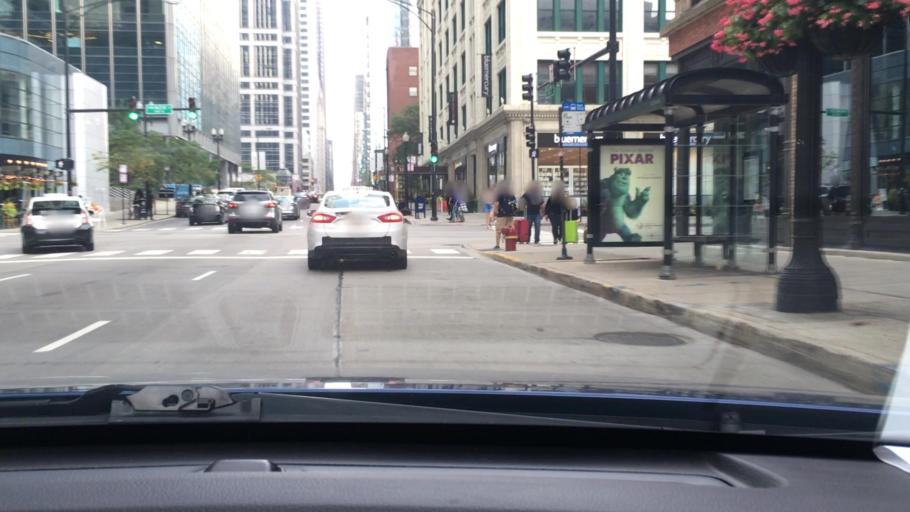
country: US
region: Illinois
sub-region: Cook County
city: Chicago
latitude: 41.8895
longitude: -87.6311
